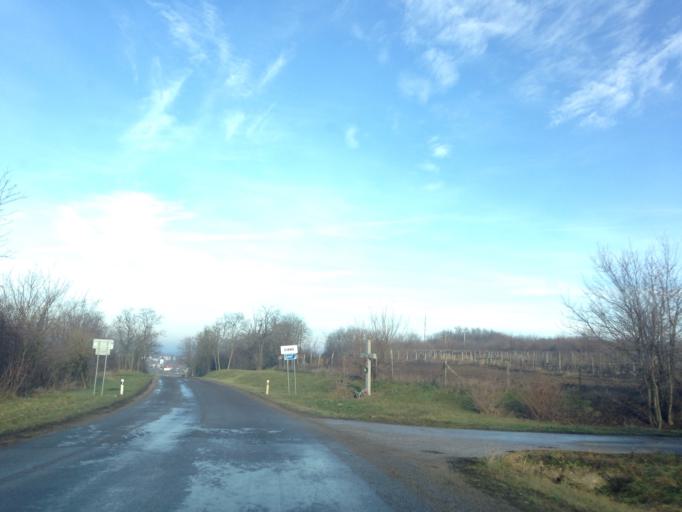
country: SK
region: Nitriansky
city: Svodin
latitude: 47.9466
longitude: 18.4142
